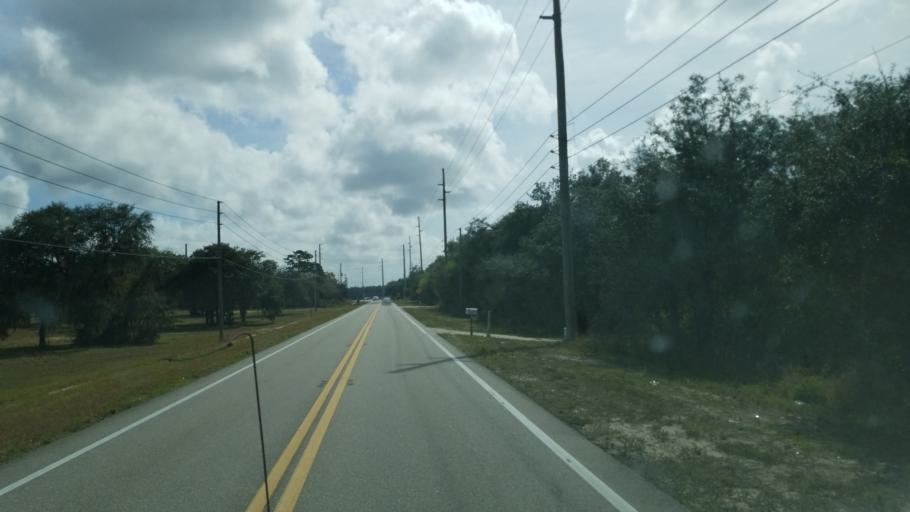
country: US
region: Florida
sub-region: Polk County
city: Dundee
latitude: 28.0370
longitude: -81.5325
